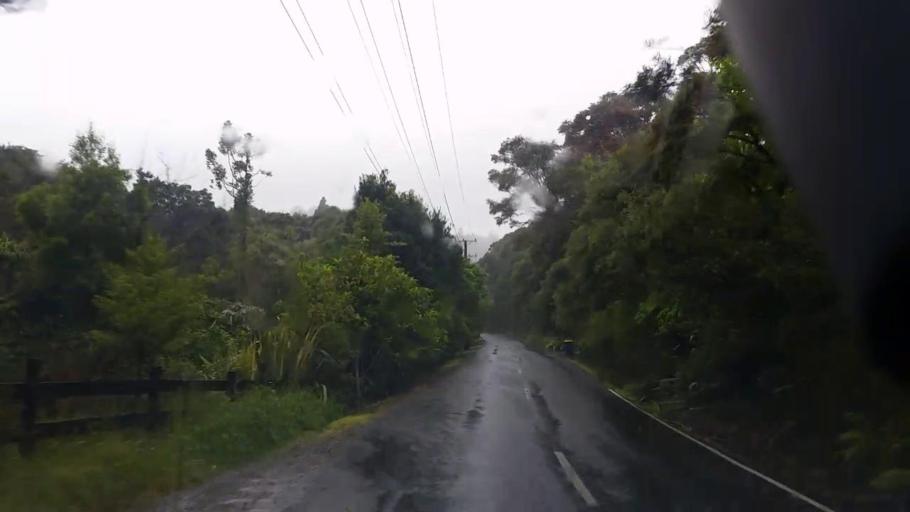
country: NZ
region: Auckland
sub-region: Auckland
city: Waitakere
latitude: -36.9064
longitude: 174.5694
